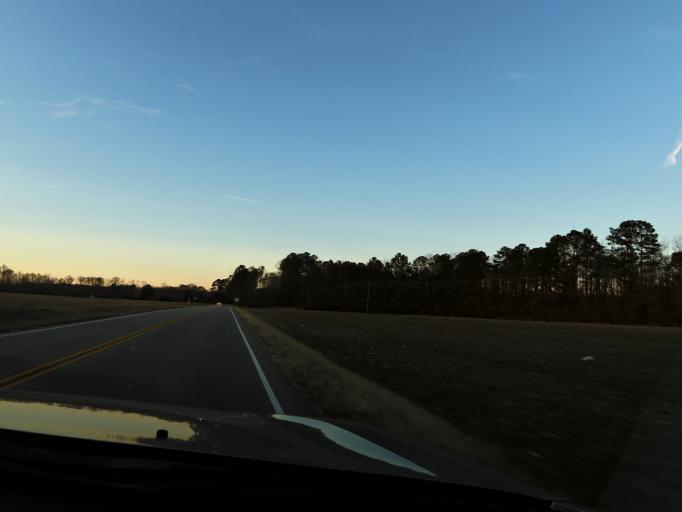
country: US
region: Virginia
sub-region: Southampton County
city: Courtland
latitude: 36.7346
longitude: -77.0743
